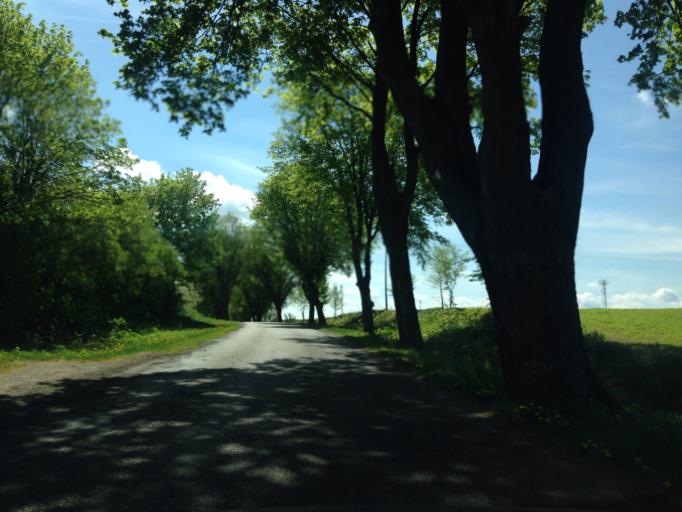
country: PL
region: Kujawsko-Pomorskie
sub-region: Powiat brodnicki
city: Gorzno
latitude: 53.2090
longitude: 19.6358
